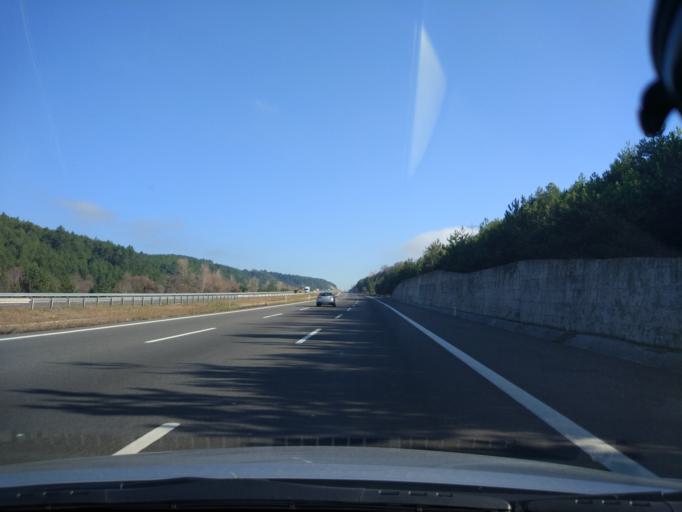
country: TR
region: Bolu
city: Yenicaga
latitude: 40.7443
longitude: 31.8711
